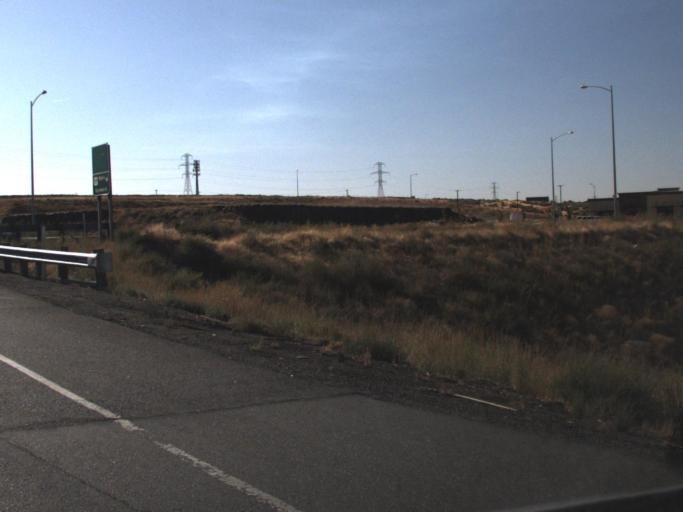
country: US
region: Washington
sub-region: Benton County
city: Kennewick
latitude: 46.1735
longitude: -119.1920
